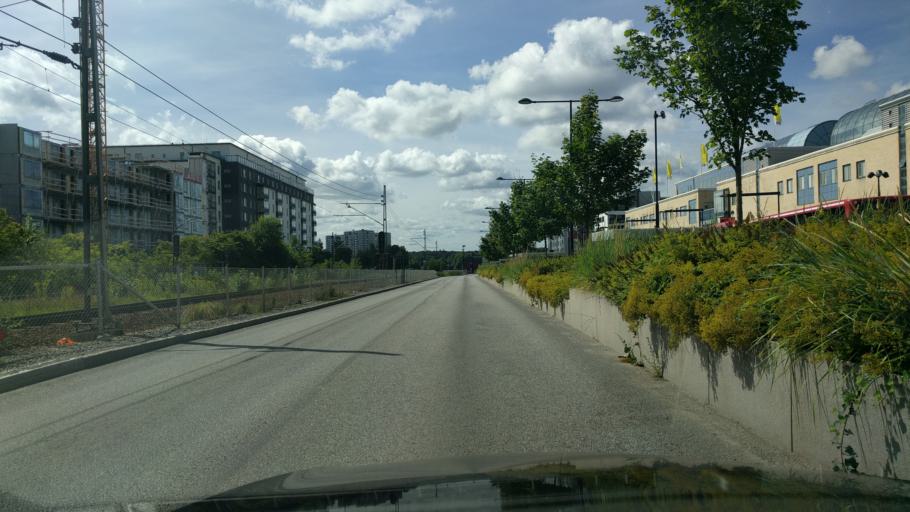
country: SE
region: Stockholm
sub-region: Taby Kommun
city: Taby
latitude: 59.4440
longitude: 18.0734
